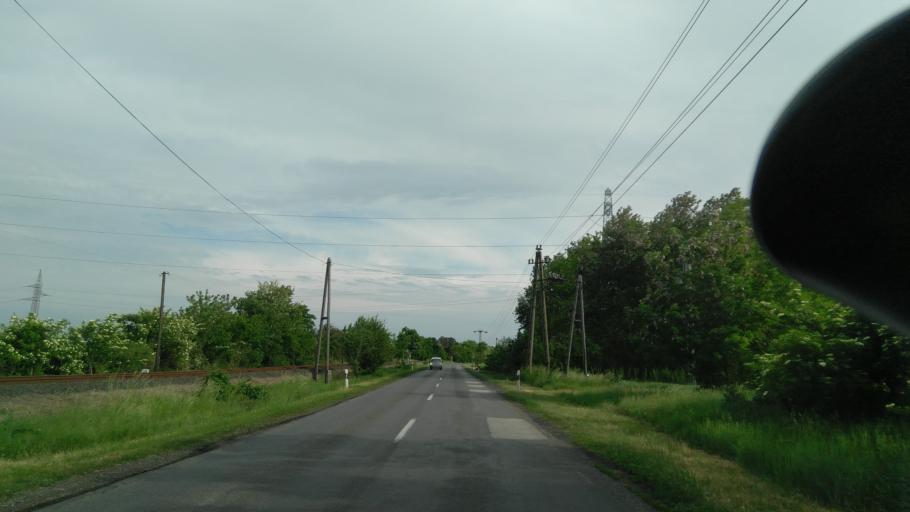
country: HU
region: Bekes
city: Oroshaza
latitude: 46.6016
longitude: 20.6811
